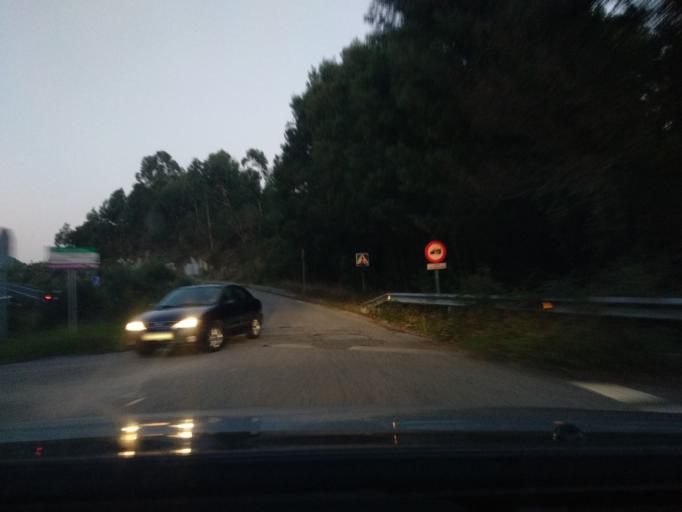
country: ES
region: Galicia
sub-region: Provincia de Pontevedra
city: Moana
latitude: 42.2844
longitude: -8.7548
